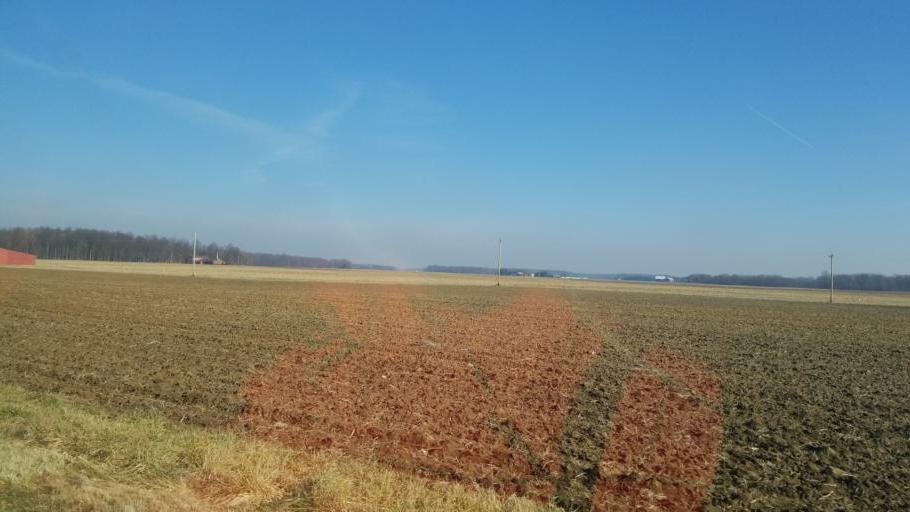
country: US
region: Ohio
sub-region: Crawford County
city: Bucyrus
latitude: 40.9599
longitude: -83.0743
